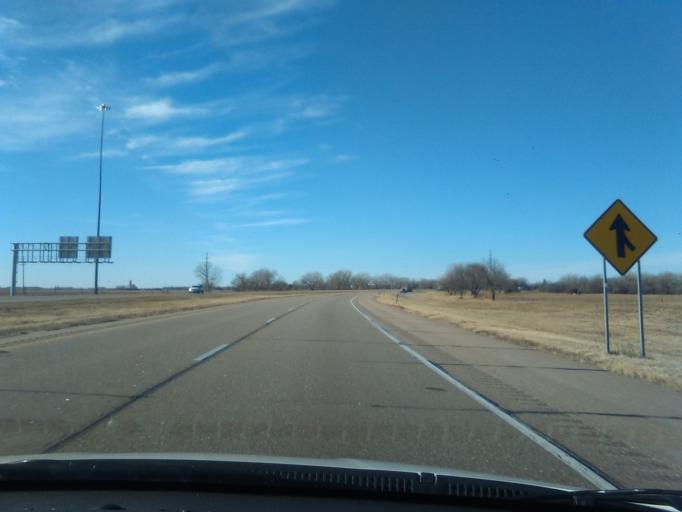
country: US
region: Nebraska
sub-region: Hall County
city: Grand Island
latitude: 40.8198
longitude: -98.3816
